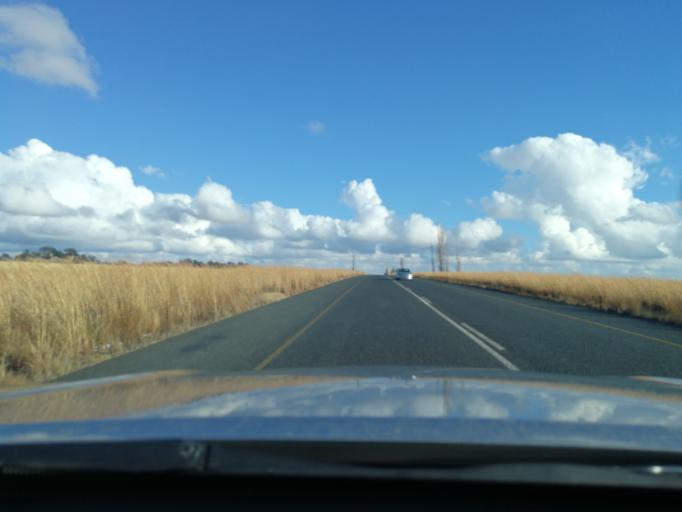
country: ZA
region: Orange Free State
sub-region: Thabo Mofutsanyana District Municipality
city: Bethlehem
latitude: -28.0662
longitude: 28.3616
